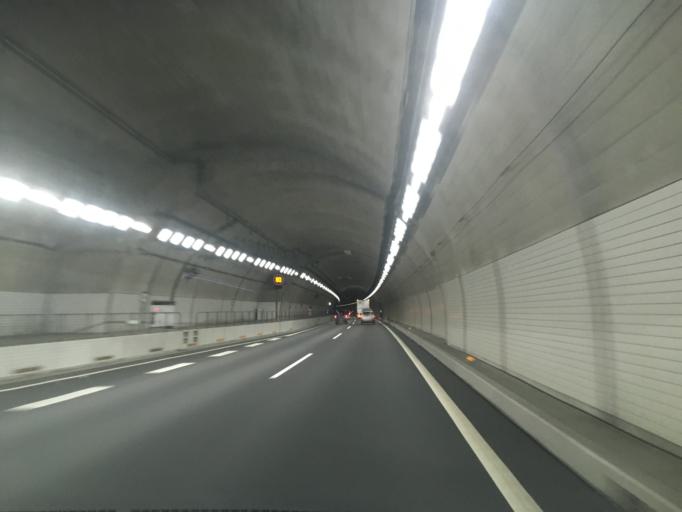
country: JP
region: Kanagawa
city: Zama
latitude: 35.5255
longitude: 139.3498
